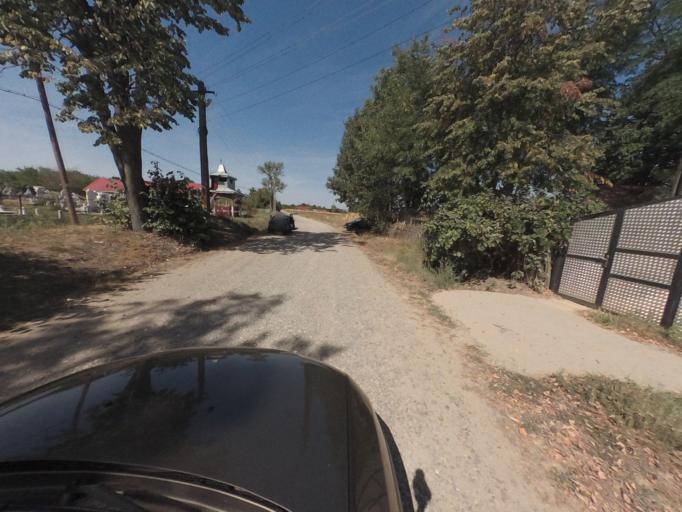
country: RO
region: Vaslui
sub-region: Comuna Deleni
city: Deleni
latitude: 46.5358
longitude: 27.7535
